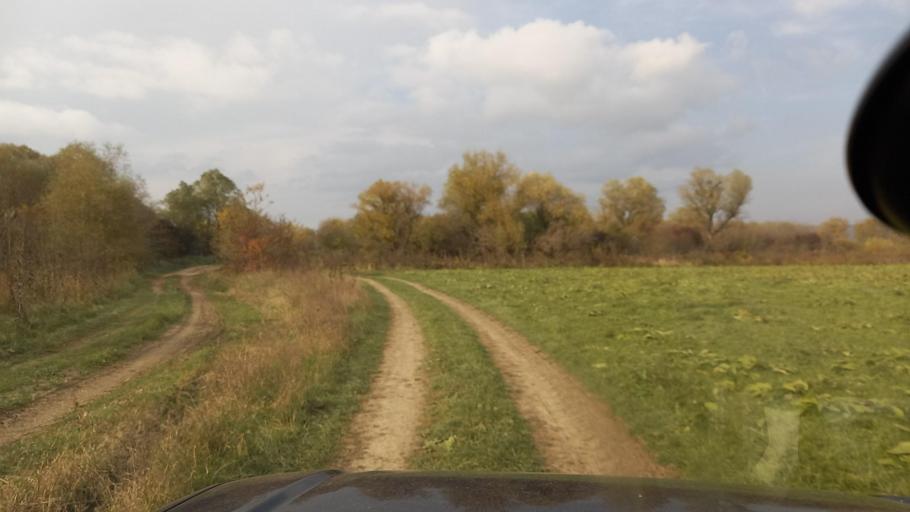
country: RU
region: Krasnodarskiy
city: Gubskaya
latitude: 44.3038
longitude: 40.5522
